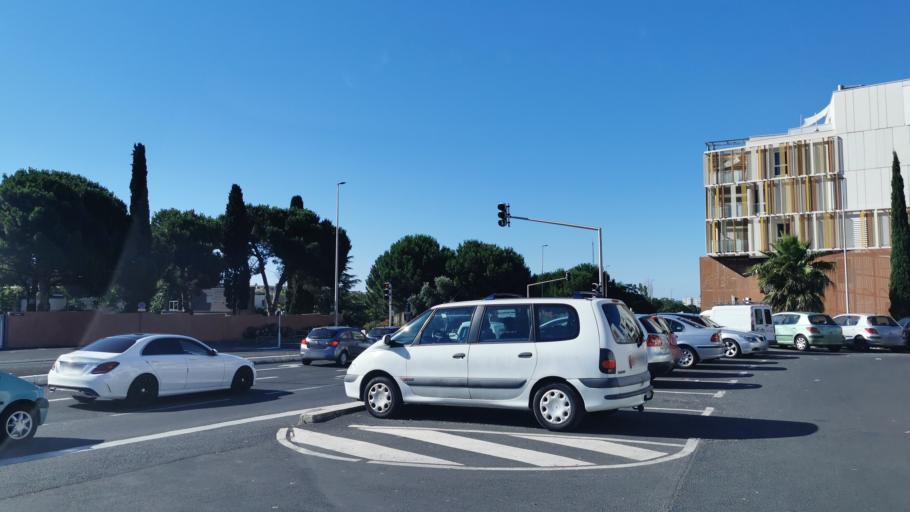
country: FR
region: Languedoc-Roussillon
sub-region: Departement de l'Herault
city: Beziers
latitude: 43.3436
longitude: 3.2380
